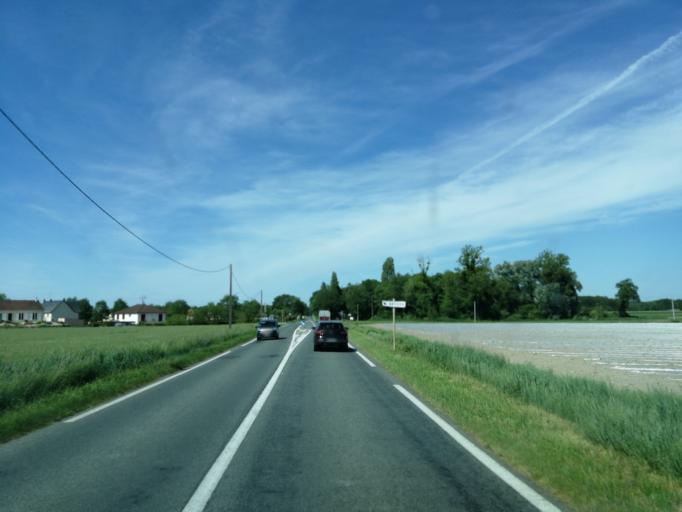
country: FR
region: Centre
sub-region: Departement d'Indre-et-Loire
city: Ligre
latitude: 47.0881
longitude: 0.1814
